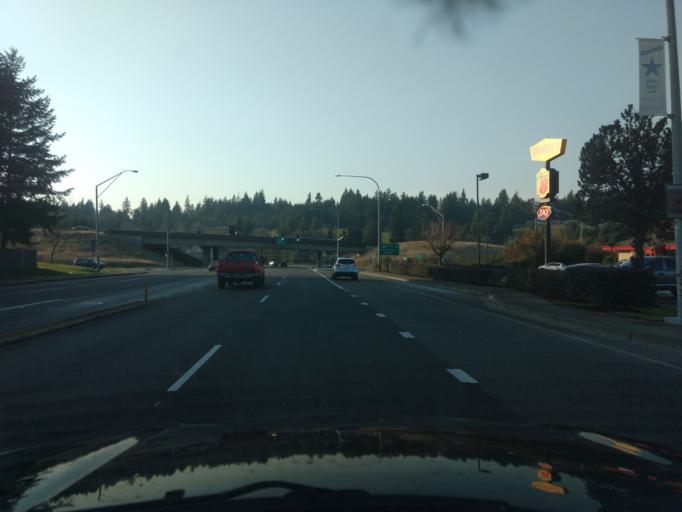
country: US
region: Washington
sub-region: Kitsap County
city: Navy Yard City
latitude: 47.5697
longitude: -122.6822
